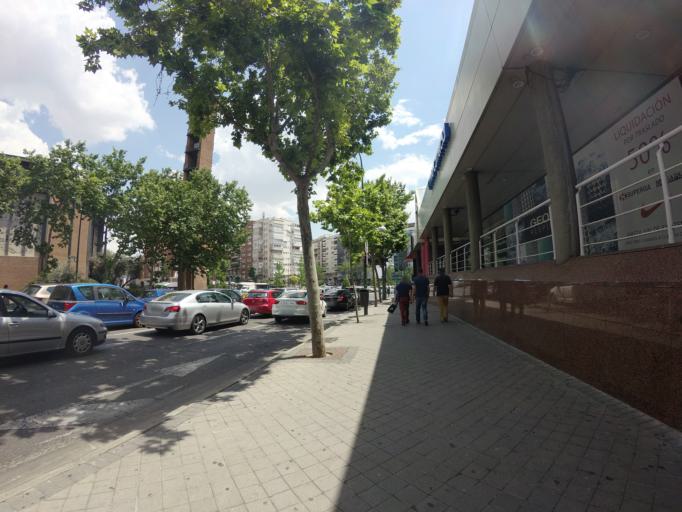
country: ES
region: Madrid
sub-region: Provincia de Madrid
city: Chamartin
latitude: 40.4524
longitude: -3.6865
